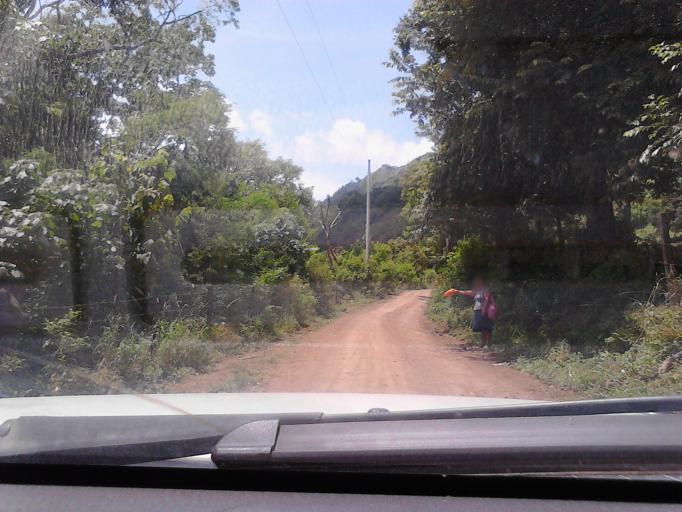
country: NI
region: Matagalpa
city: Terrabona
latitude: 12.7149
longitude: -85.9402
